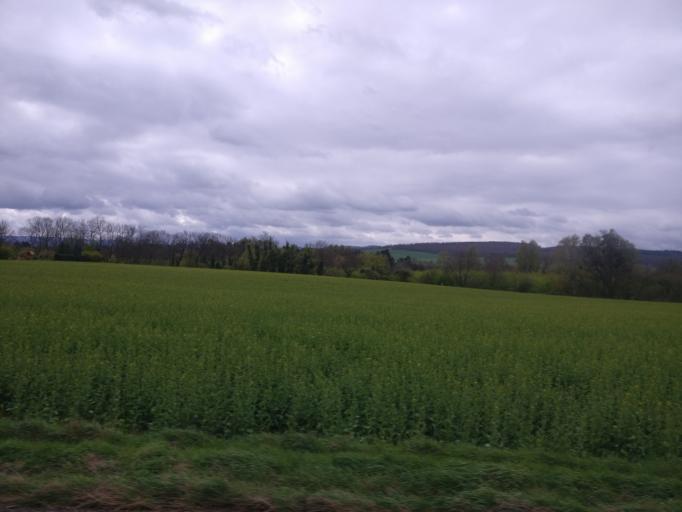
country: DE
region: Lower Saxony
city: Alt Wallmoden
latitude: 52.0271
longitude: 10.3471
